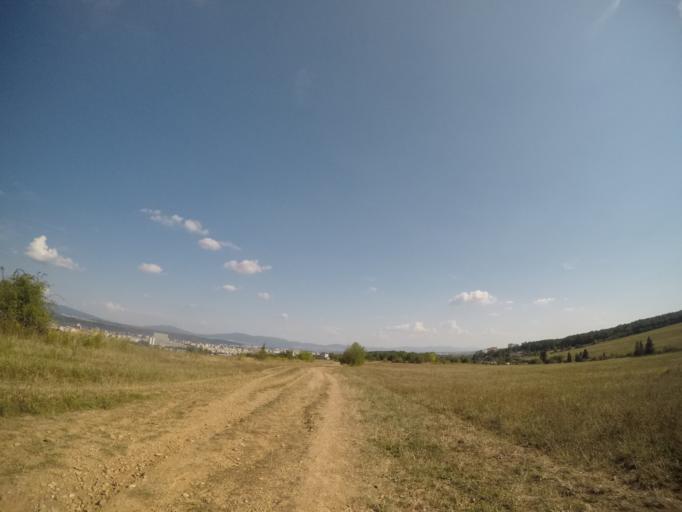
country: SK
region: Kosicky
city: Kosice
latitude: 48.7294
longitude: 21.2166
